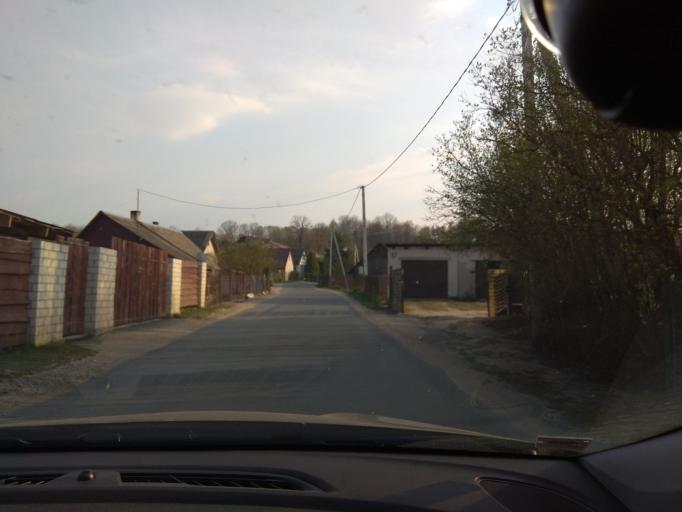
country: LT
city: Baltoji Voke
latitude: 54.5955
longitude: 25.1754
